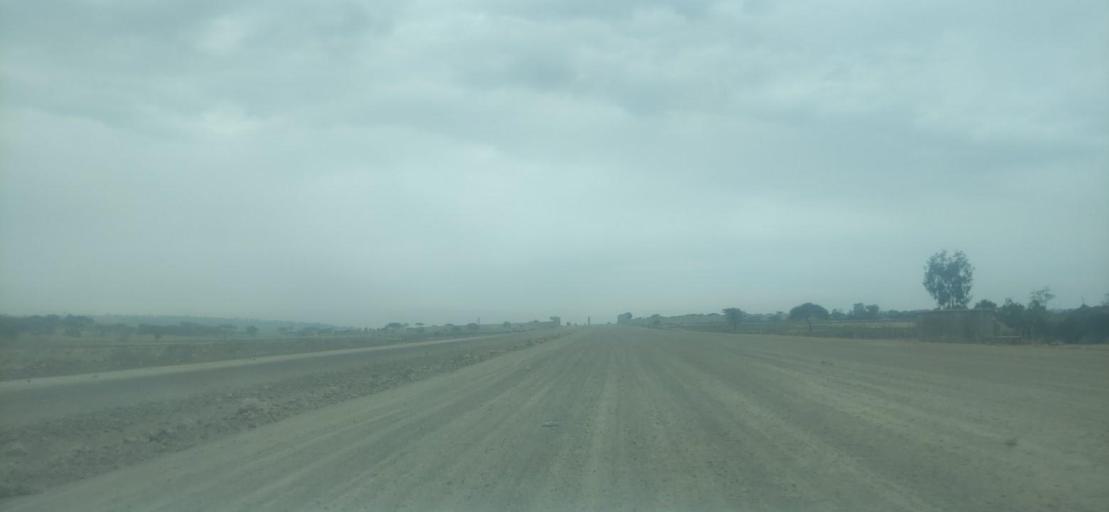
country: ET
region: Oromiya
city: Shashemene
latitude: 7.4371
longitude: 38.6719
